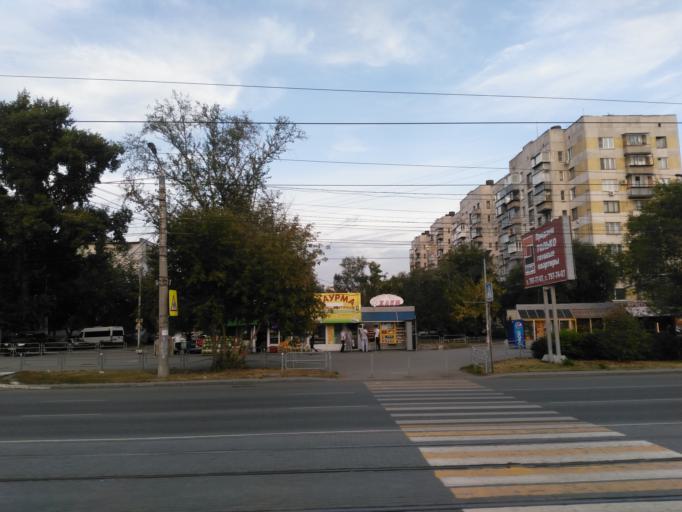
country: RU
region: Chelyabinsk
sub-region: Gorod Chelyabinsk
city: Chelyabinsk
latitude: 55.1768
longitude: 61.3994
